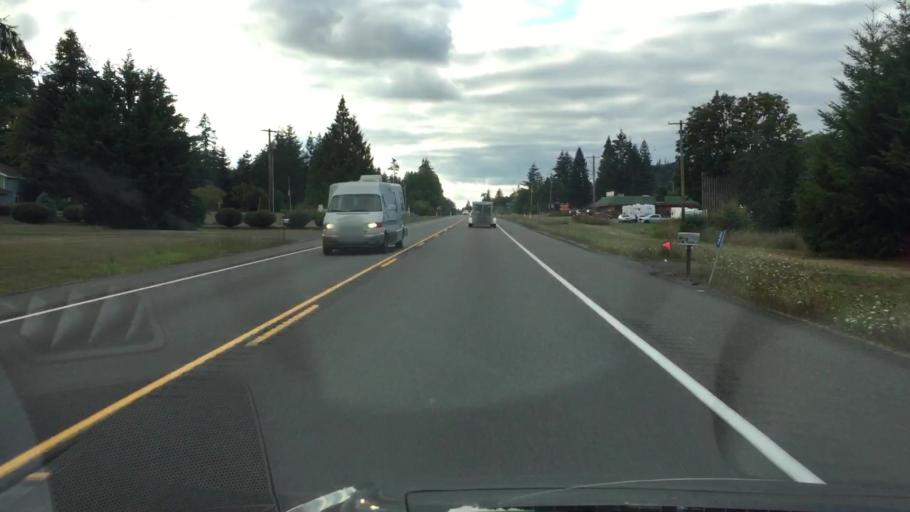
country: US
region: Washington
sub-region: Lewis County
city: Morton
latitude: 46.5210
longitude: -122.5868
